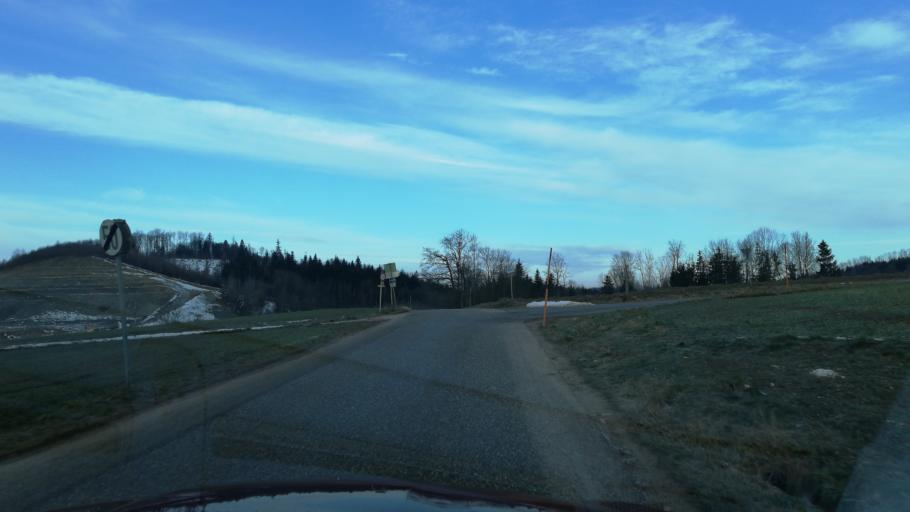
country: AT
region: Upper Austria
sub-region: Wels-Land
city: Buchkirchen
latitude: 48.2336
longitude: 13.9969
